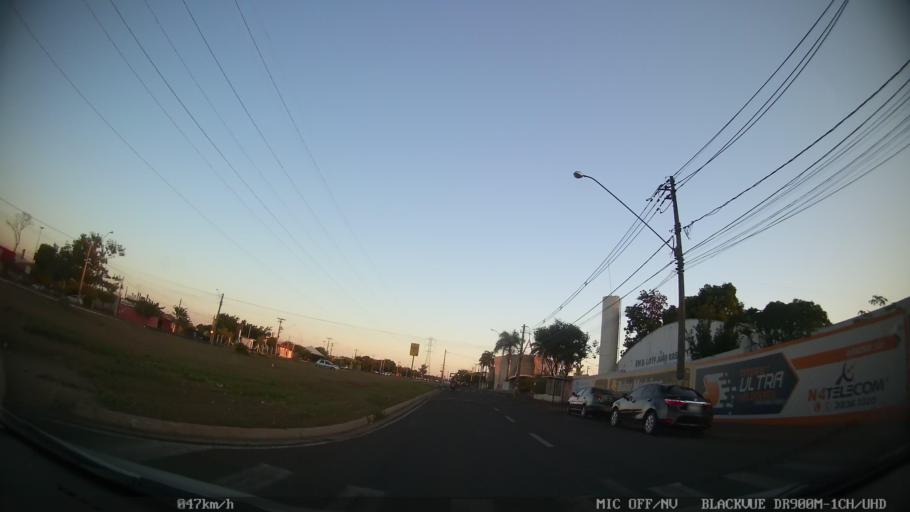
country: BR
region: Sao Paulo
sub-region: Sao Jose Do Rio Preto
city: Sao Jose do Rio Preto
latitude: -20.7908
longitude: -49.3445
